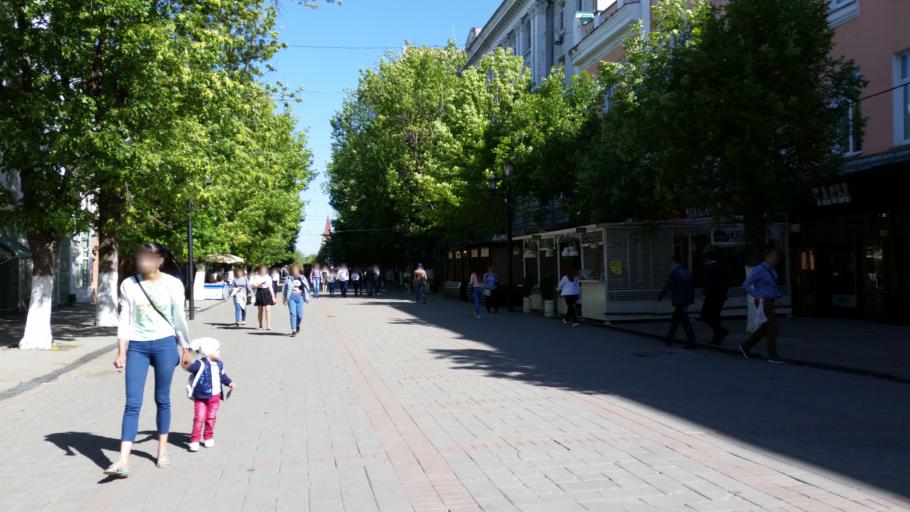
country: RU
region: Saratov
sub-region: Saratovskiy Rayon
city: Saratov
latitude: 51.5315
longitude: 46.0274
